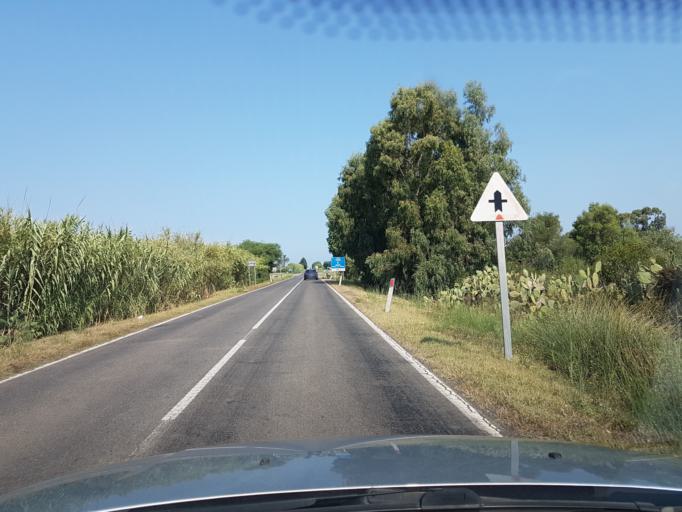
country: IT
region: Sardinia
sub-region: Provincia di Oristano
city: Donigala Fenugheddu
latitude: 39.9498
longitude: 8.5617
